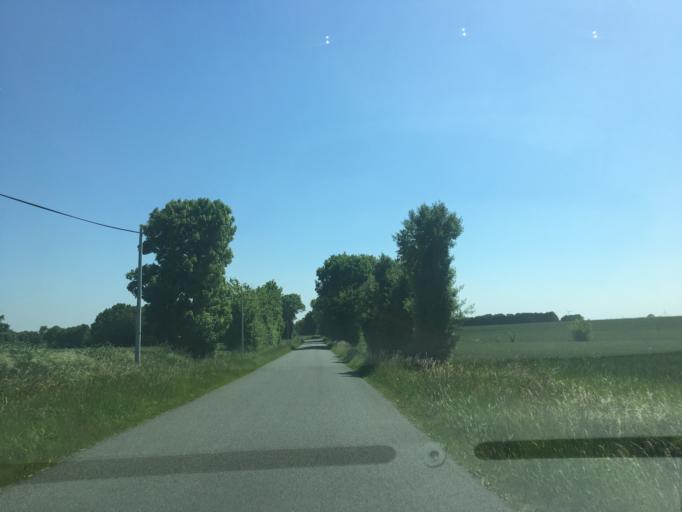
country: FR
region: Poitou-Charentes
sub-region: Departement des Deux-Sevres
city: Beauvoir-sur-Niort
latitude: 46.0837
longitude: -0.5587
